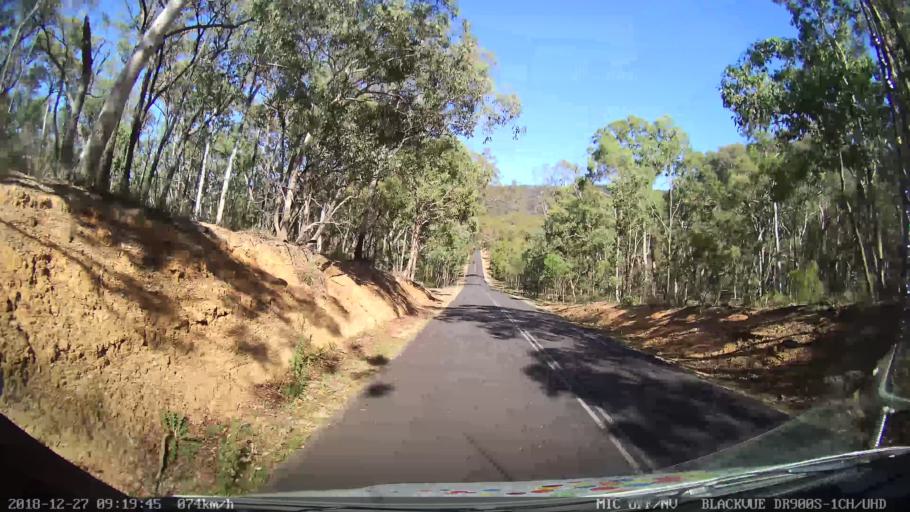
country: AU
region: New South Wales
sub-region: Lithgow
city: Portland
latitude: -33.1188
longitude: 150.0324
